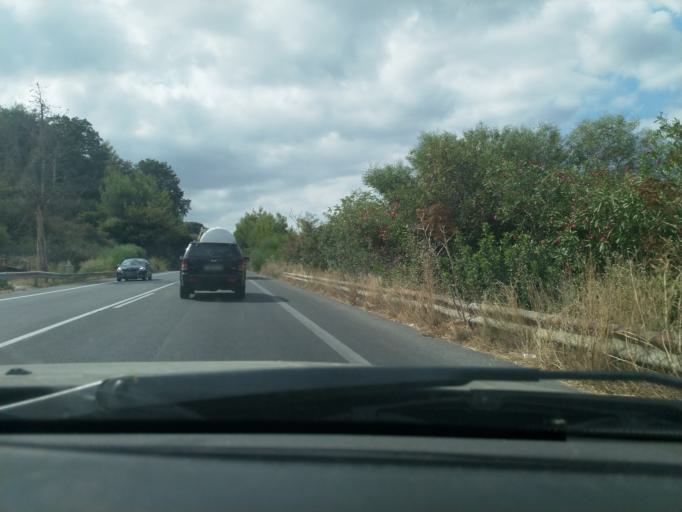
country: GR
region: Crete
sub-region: Nomos Chanias
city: Georgioupolis
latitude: 35.3619
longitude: 24.2460
